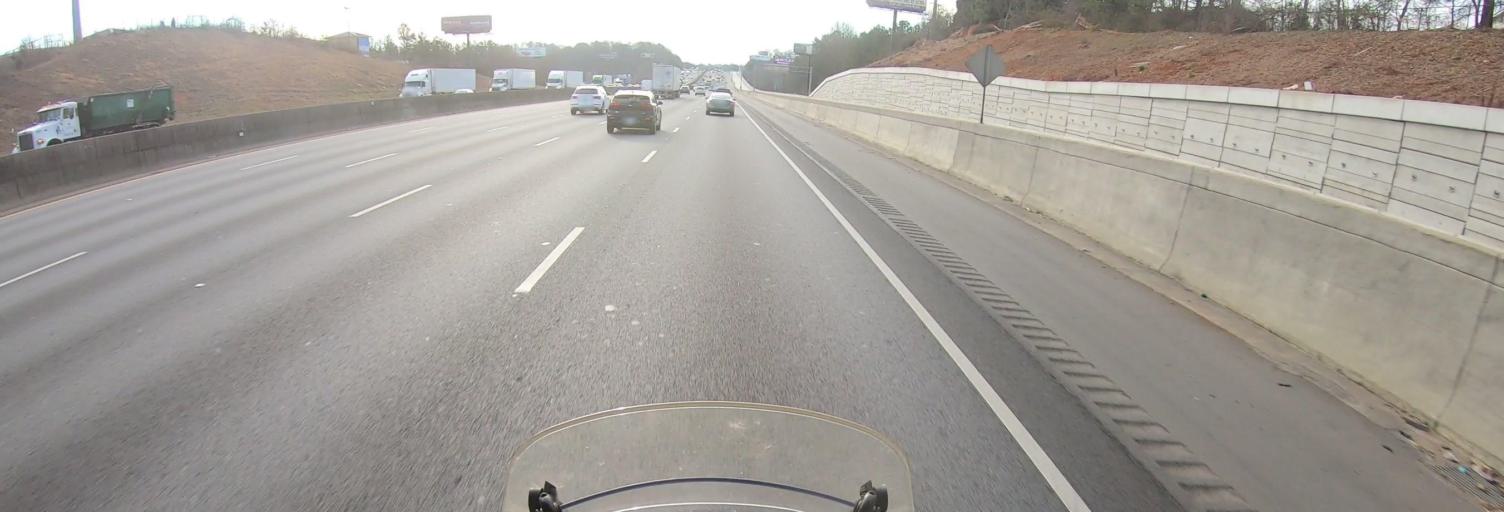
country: US
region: Georgia
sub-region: Cobb County
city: Marietta
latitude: 33.9711
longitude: -84.5316
